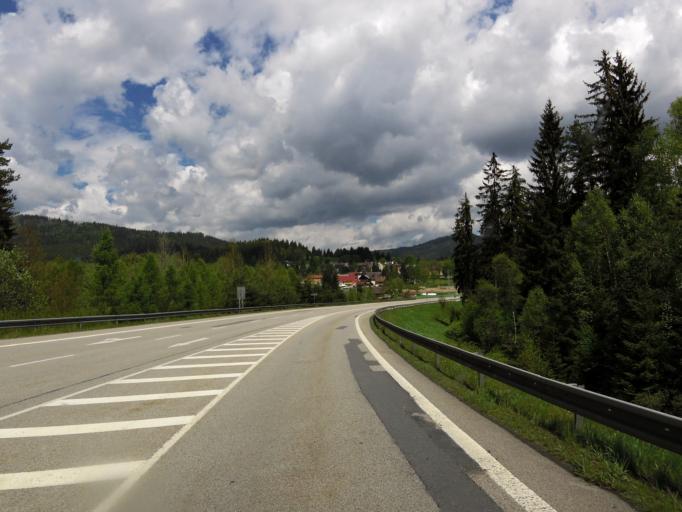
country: DE
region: Bavaria
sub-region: Lower Bavaria
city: Philippsreut
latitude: 48.9025
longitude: 13.7202
